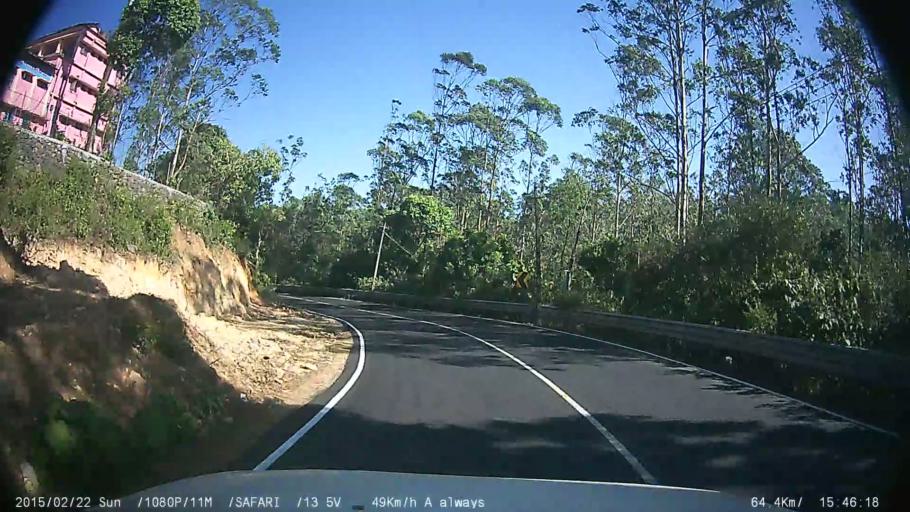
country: IN
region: Kerala
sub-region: Kottayam
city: Erattupetta
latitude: 9.5796
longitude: 76.9828
